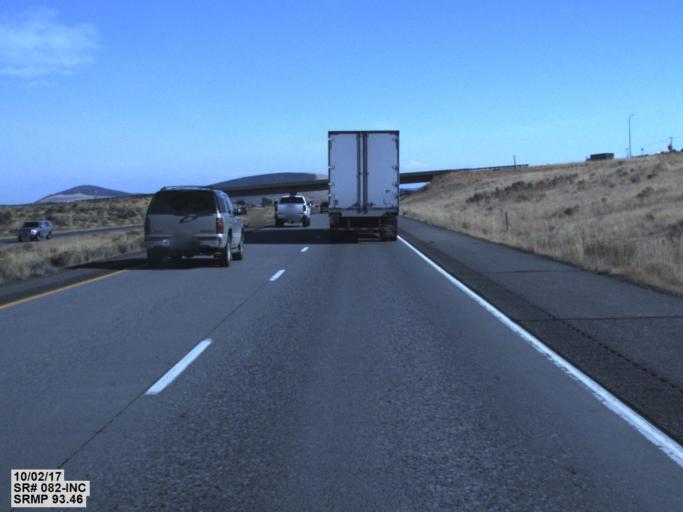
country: US
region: Washington
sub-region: Benton County
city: Benton City
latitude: 46.2644
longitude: -119.5378
